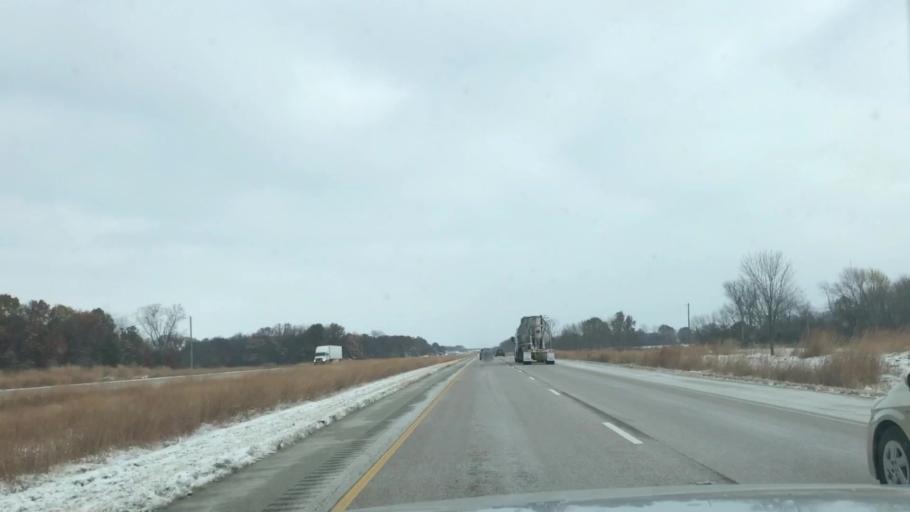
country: US
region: Illinois
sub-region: Macoupin County
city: Mount Olive
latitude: 39.1075
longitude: -89.7292
